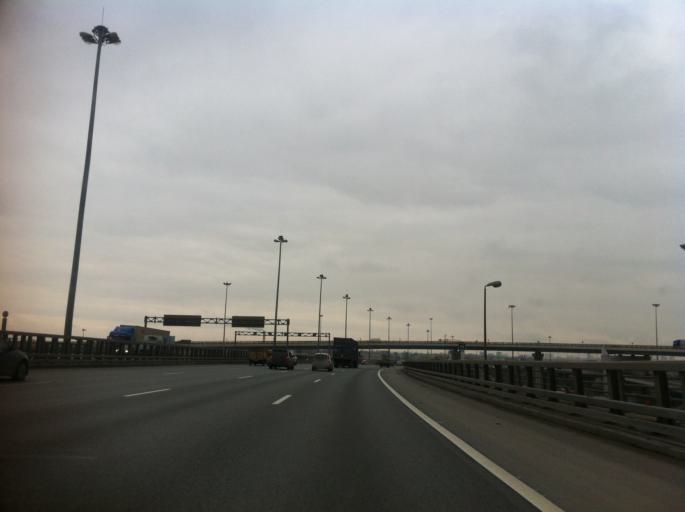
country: RU
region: St.-Petersburg
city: Kupchino
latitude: 59.8105
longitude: 30.3278
